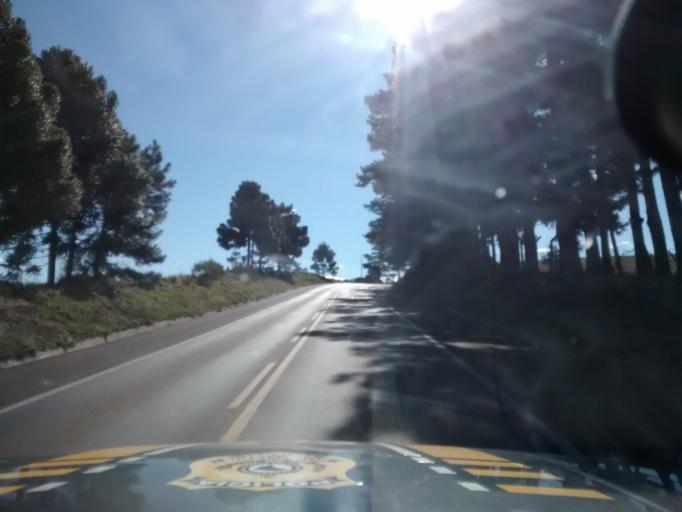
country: BR
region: Rio Grande do Sul
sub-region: Lagoa Vermelha
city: Lagoa Vermelha
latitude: -28.3088
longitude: -51.3653
